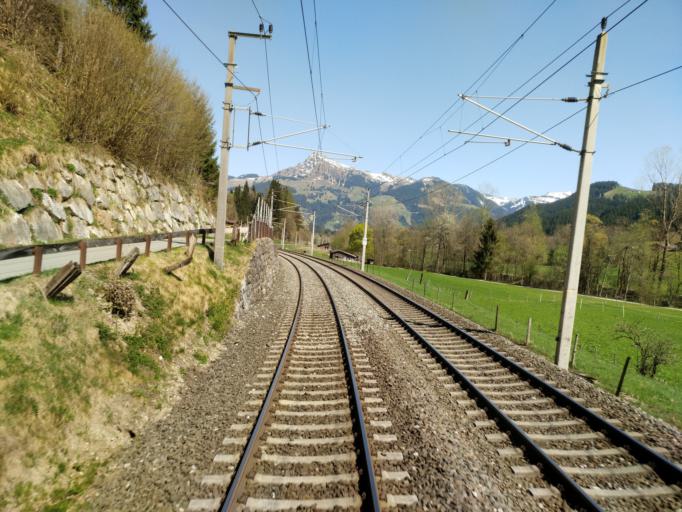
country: AT
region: Tyrol
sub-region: Politischer Bezirk Kitzbuhel
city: Kirchberg in Tirol
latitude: 47.4524
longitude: 12.3295
